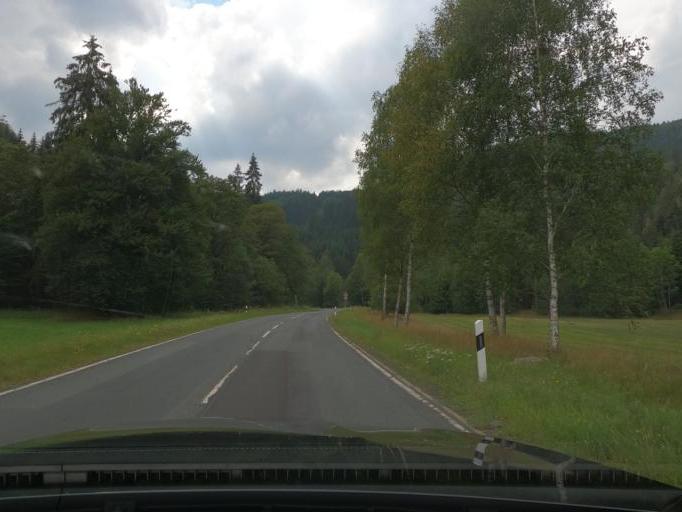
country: DE
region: Lower Saxony
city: Wildemann
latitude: 51.8587
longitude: 10.2722
